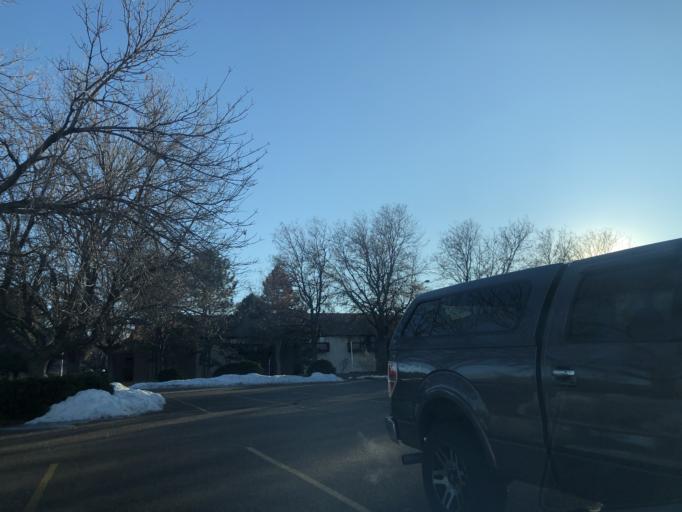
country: US
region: Colorado
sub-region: Adams County
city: Aurora
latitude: 39.7203
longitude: -104.8153
